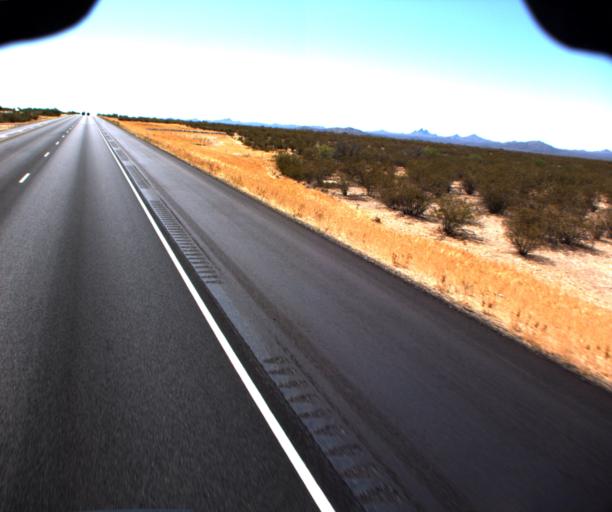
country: US
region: Arizona
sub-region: Yavapai County
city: Congress
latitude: 34.0735
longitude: -112.8794
